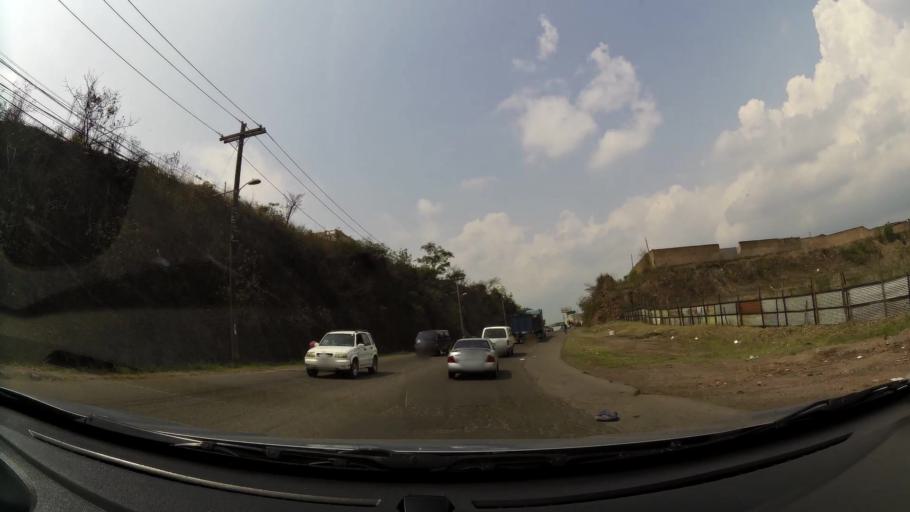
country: HN
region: Francisco Morazan
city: El Lolo
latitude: 14.1223
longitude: -87.2258
